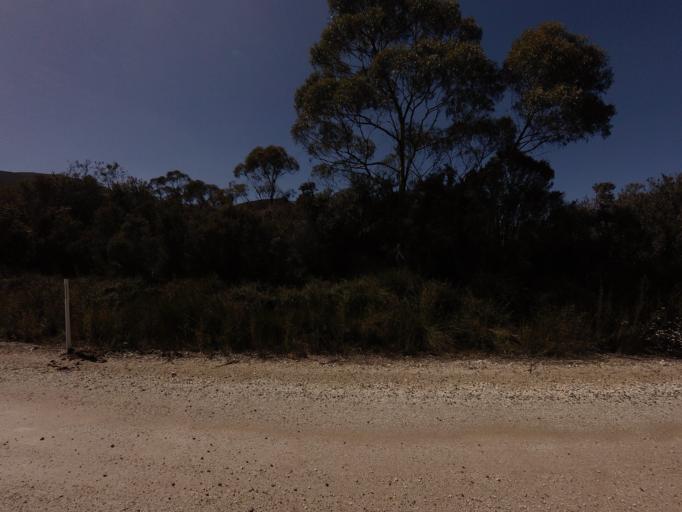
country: AU
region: Tasmania
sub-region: Huon Valley
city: Geeveston
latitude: -42.9593
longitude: 146.3615
